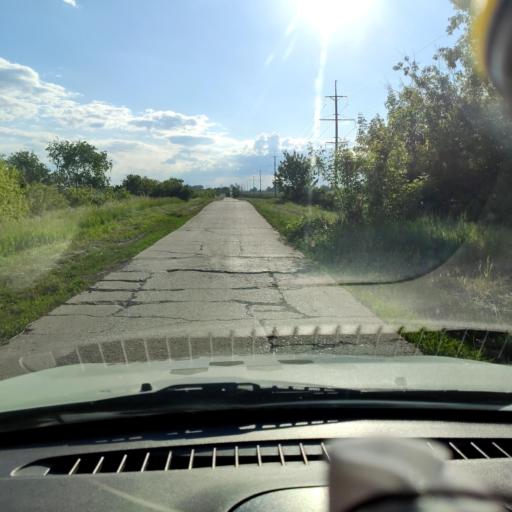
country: RU
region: Samara
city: Tol'yatti
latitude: 53.5868
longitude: 49.4301
